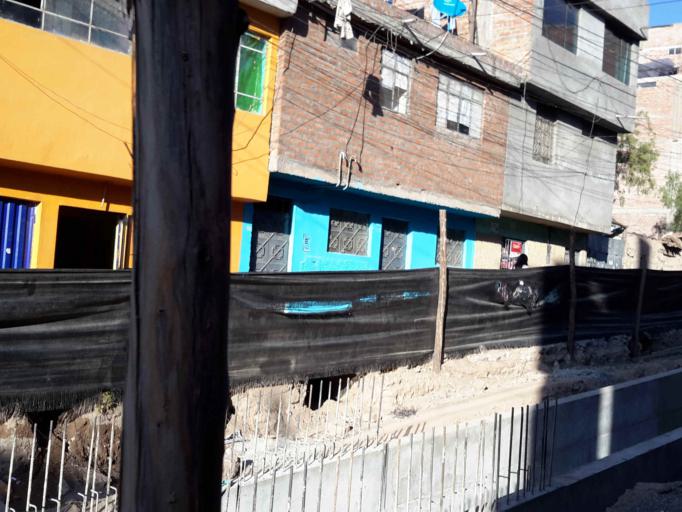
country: PE
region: Ayacucho
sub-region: Provincia de Huamanga
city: Ayacucho
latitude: -13.1543
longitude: -74.2269
